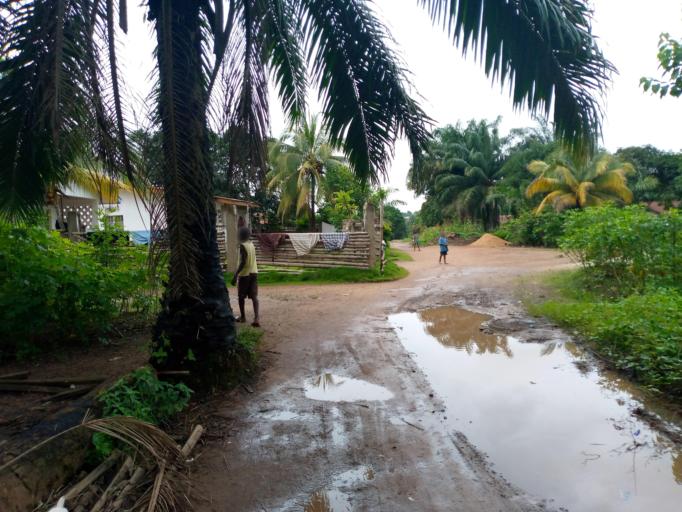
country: SL
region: Eastern Province
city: Kenema
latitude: 7.8476
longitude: -11.2039
